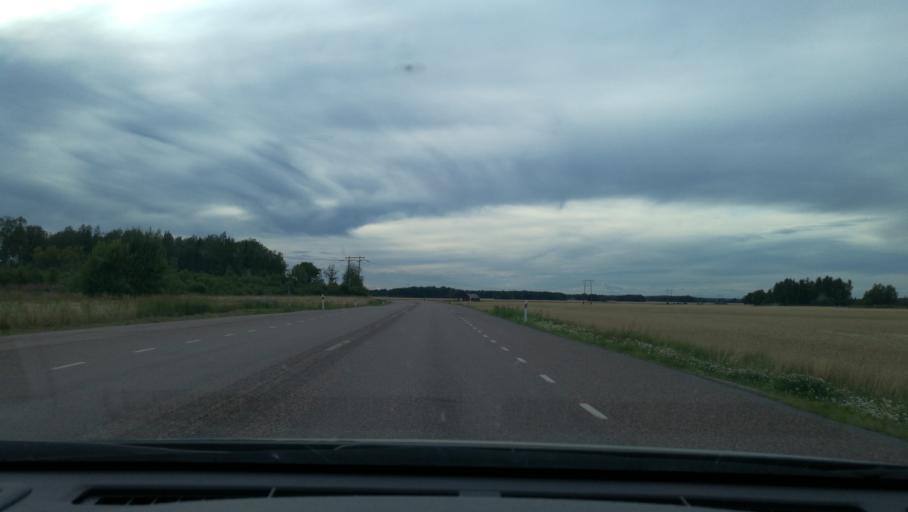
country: SE
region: Vaestmanland
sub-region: Kopings Kommun
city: Koping
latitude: 59.4542
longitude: 16.0260
